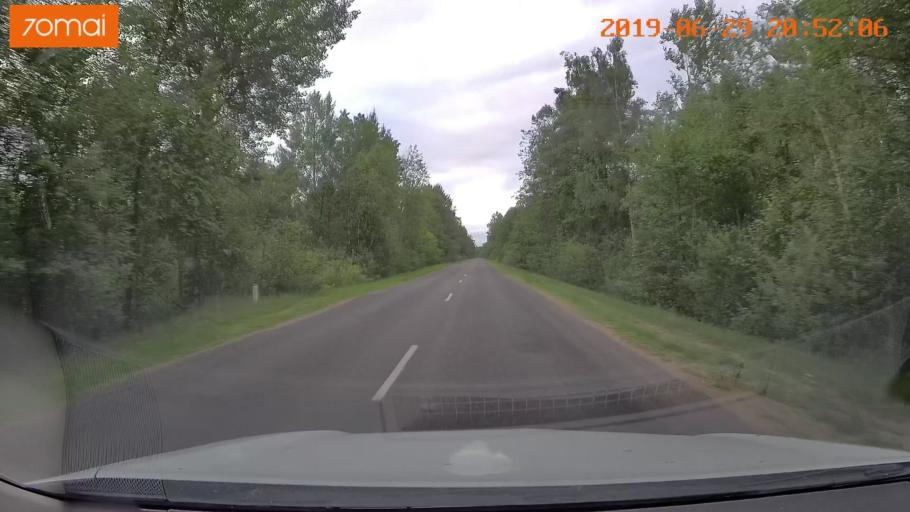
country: BY
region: Brest
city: Hantsavichy
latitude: 52.6957
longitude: 26.3585
